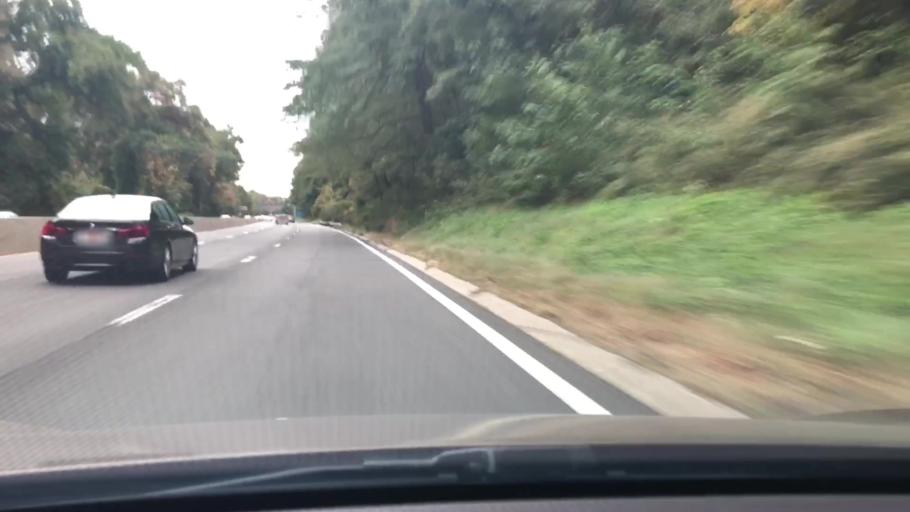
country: US
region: New York
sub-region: Westchester County
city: Yonkers
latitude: 40.9191
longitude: -73.8829
